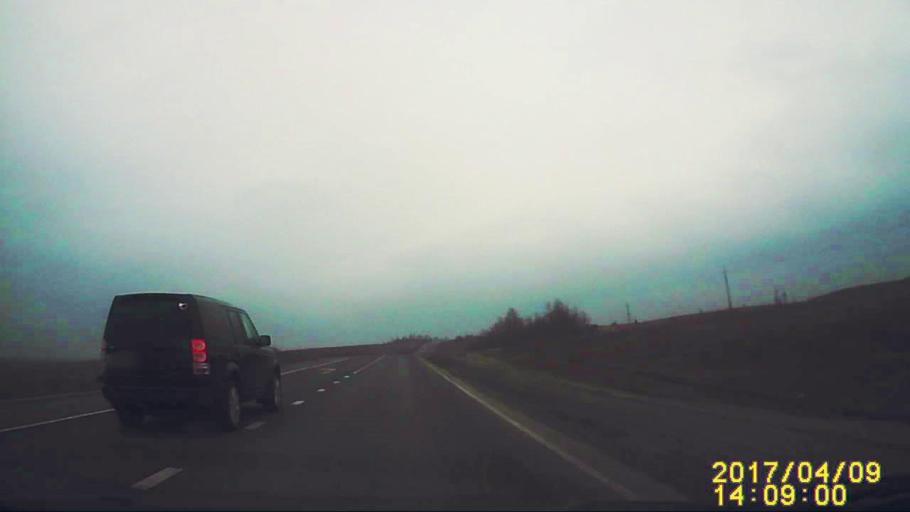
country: RU
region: Ulyanovsk
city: Silikatnyy
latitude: 54.0245
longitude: 48.2143
